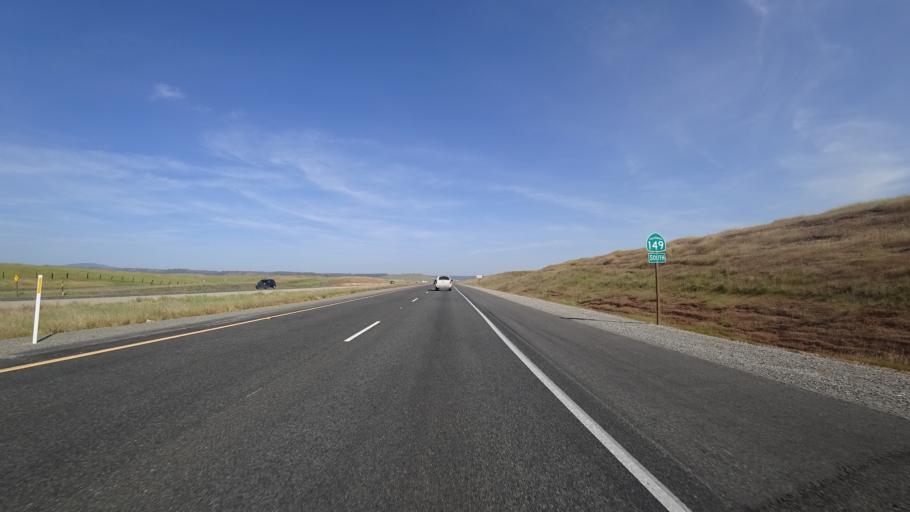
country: US
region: California
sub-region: Butte County
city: Thermalito
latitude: 39.5995
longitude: -121.6585
